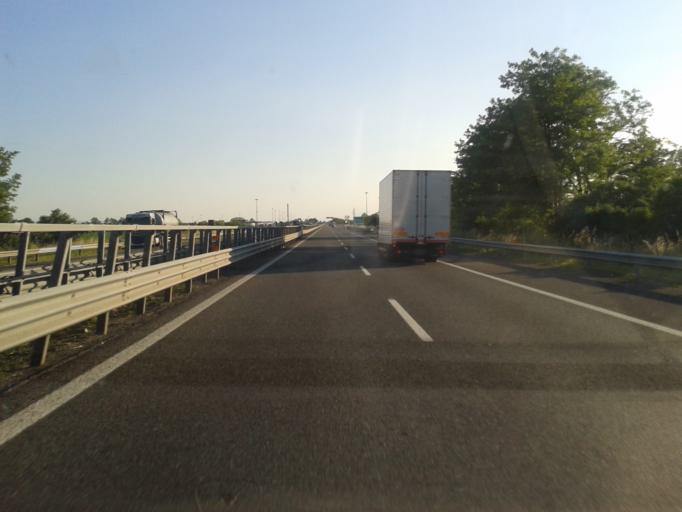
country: IT
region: Piedmont
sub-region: Provincia di Alessandria
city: Pozzolo Formigaro
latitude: 44.8046
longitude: 8.7565
